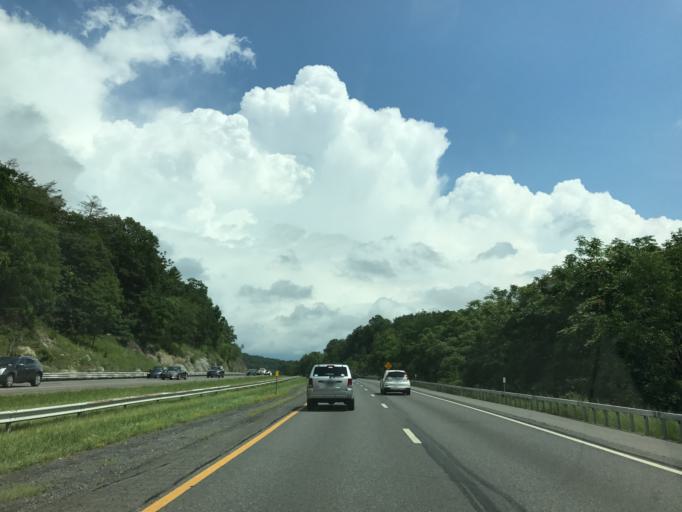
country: US
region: New York
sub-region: Greene County
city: Coxsackie
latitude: 42.3561
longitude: -73.8495
